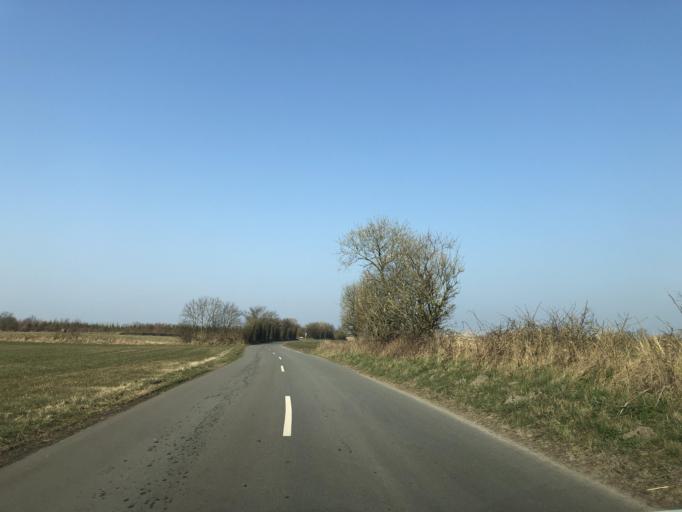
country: DK
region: South Denmark
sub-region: Sonderborg Kommune
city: Nordborg
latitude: 55.0689
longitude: 9.7312
